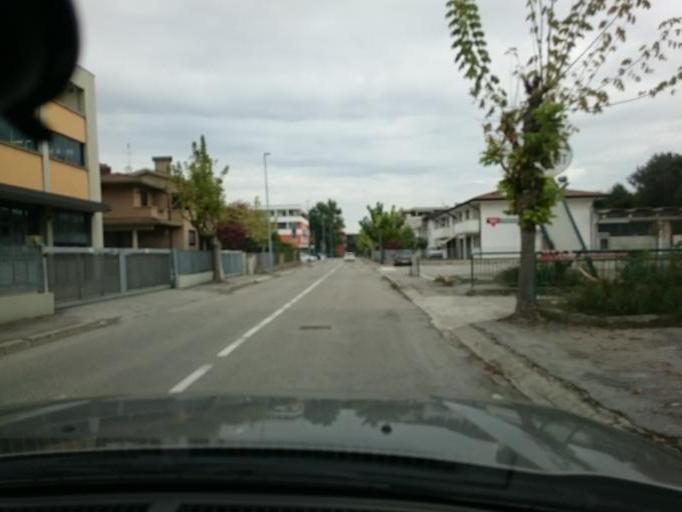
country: IT
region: Veneto
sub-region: Provincia di Padova
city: Ponte San Nicolo
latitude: 45.3763
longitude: 11.9137
